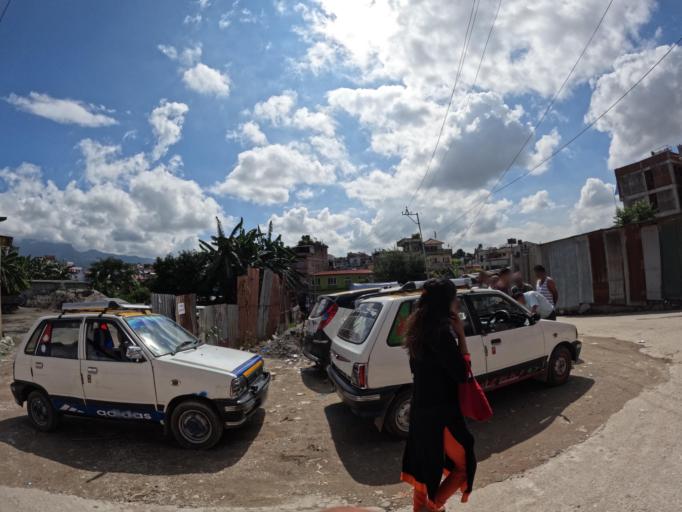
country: NP
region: Central Region
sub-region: Bagmati Zone
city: Kathmandu
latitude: 27.7444
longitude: 85.3332
